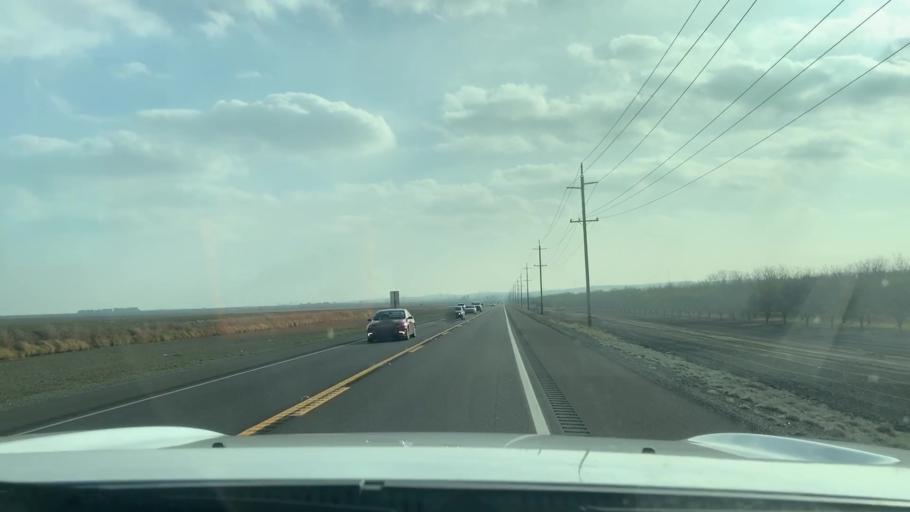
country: US
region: California
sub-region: Kings County
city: Kettleman City
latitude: 36.0337
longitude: -119.9590
